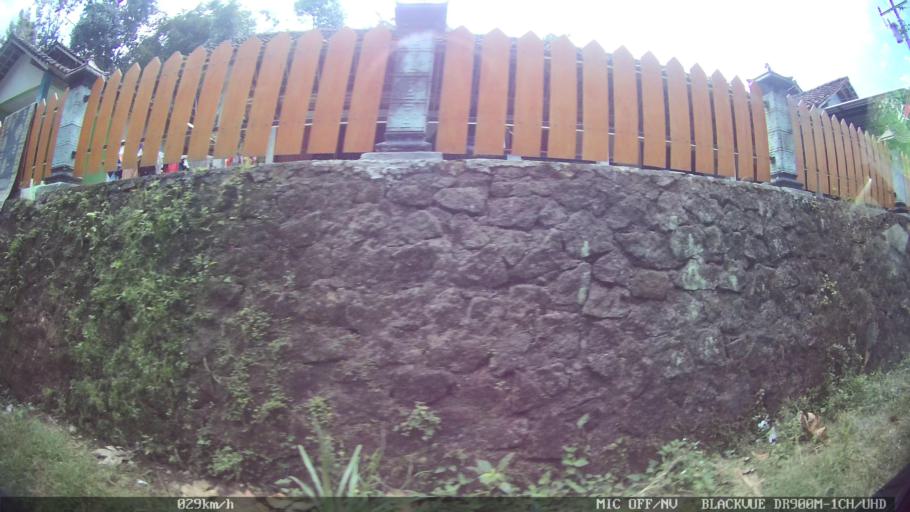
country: ID
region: Central Java
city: Candi Prambanan
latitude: -7.8189
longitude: 110.5216
